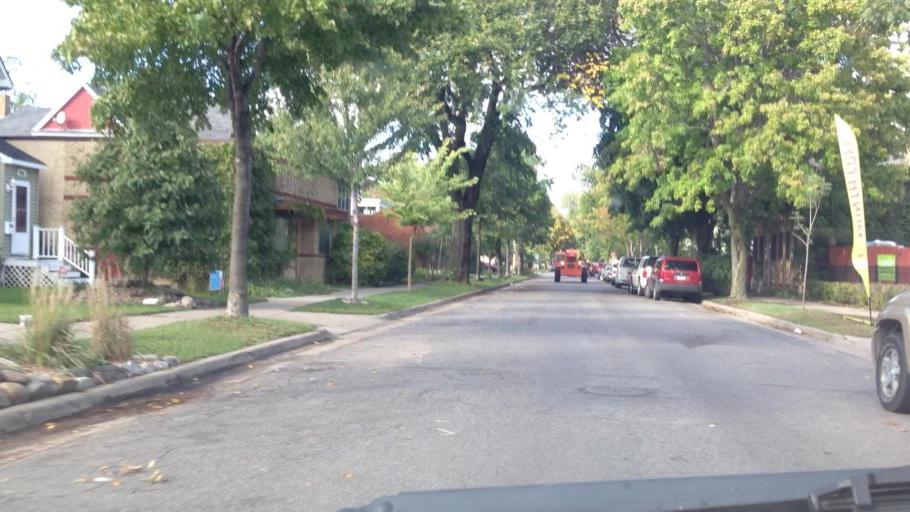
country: US
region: Minnesota
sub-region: Hennepin County
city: Minneapolis
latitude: 44.9507
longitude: -93.2855
